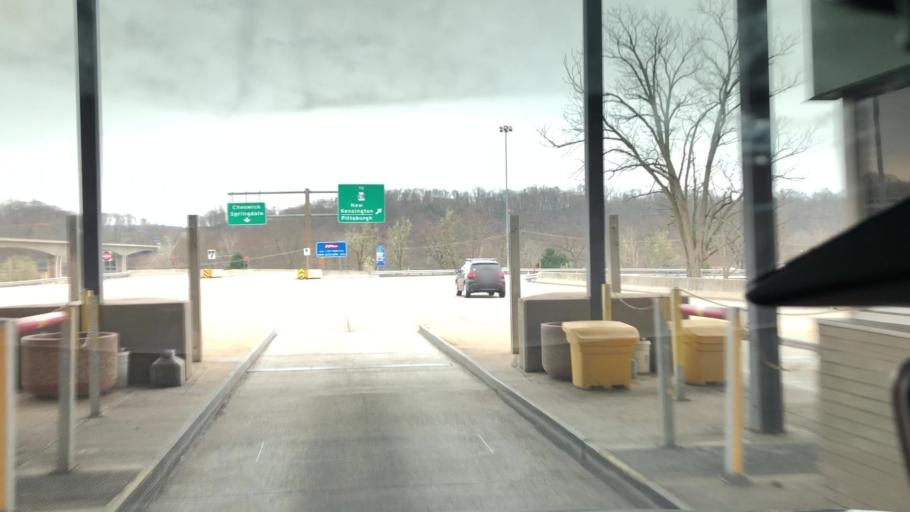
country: US
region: Pennsylvania
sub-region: Allegheny County
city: Oakmont
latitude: 40.5414
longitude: -79.8255
